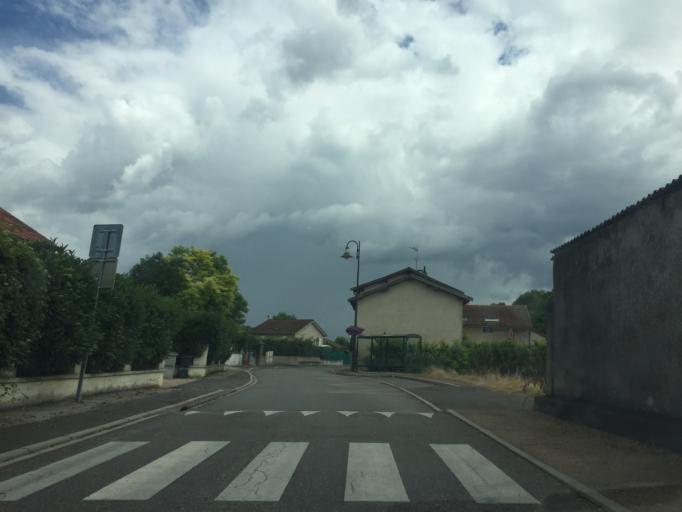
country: FR
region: Rhone-Alpes
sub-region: Departement de l'Ain
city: Nievroz
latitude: 45.8230
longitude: 5.0609
